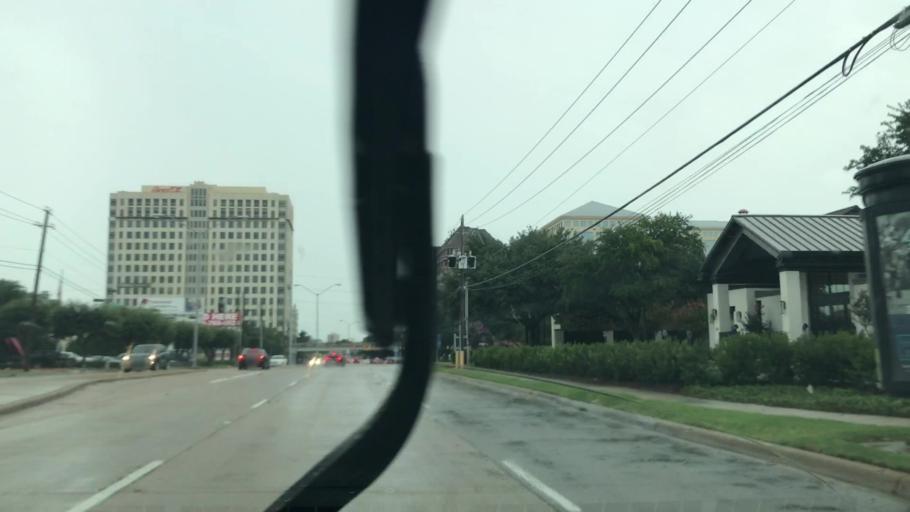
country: US
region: Texas
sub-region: Dallas County
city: Addison
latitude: 32.9395
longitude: -96.8189
